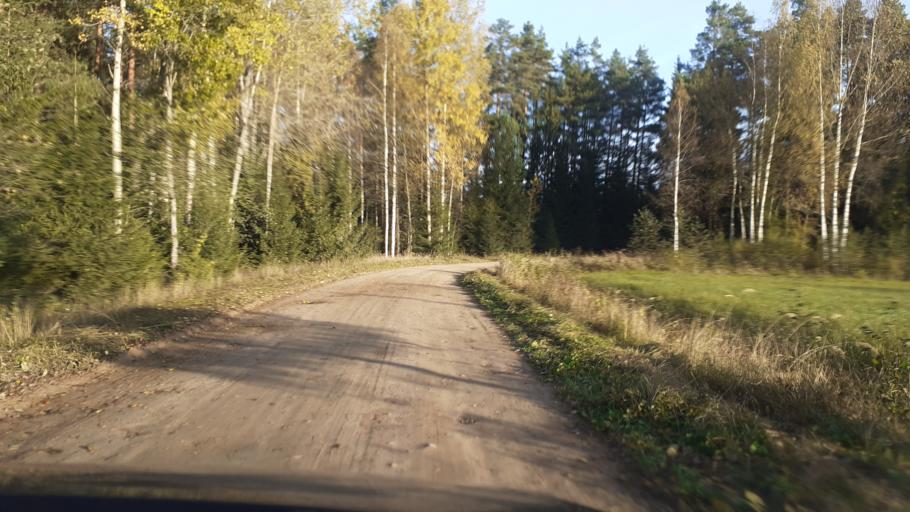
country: LV
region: Kuldigas Rajons
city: Kuldiga
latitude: 56.8665
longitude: 22.0957
